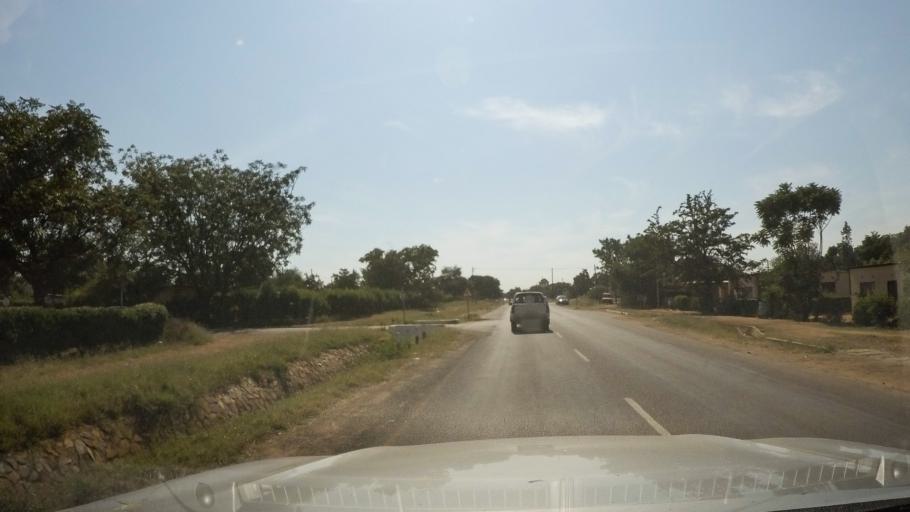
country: BW
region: South East
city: Lobatse
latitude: -25.2084
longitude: 25.6835
